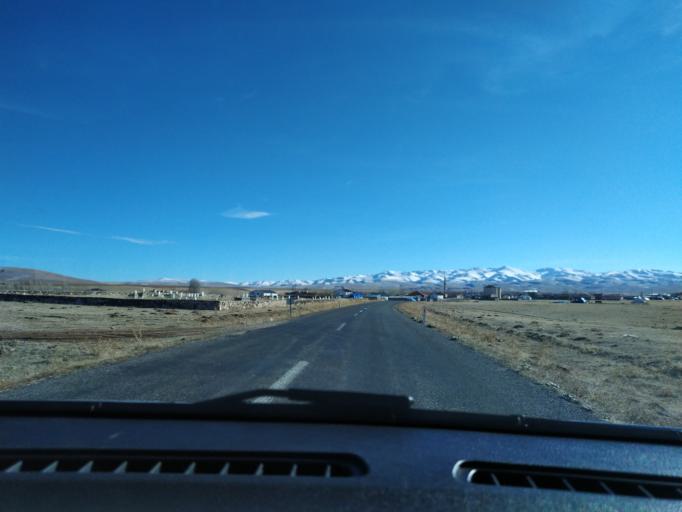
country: TR
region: Kayseri
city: Orensehir
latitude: 38.9162
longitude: 36.7313
